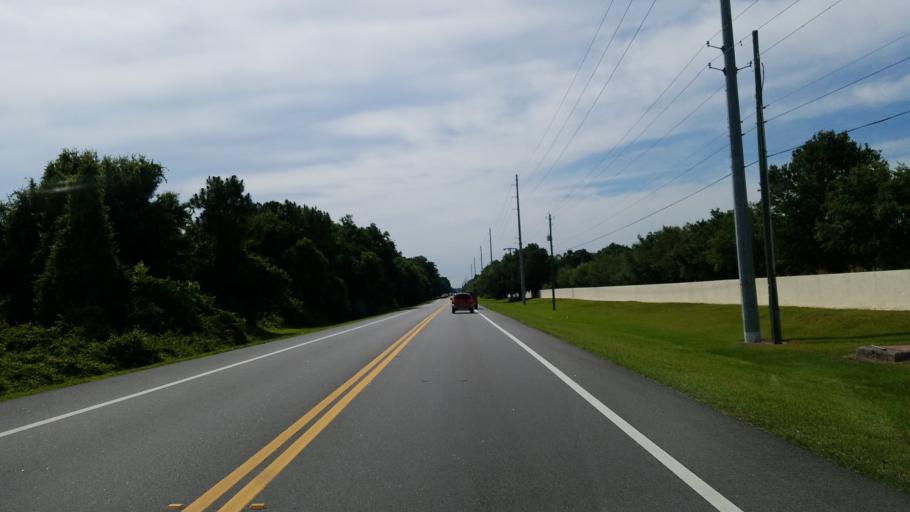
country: US
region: Florida
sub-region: Hillsborough County
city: Fish Hawk
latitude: 27.8513
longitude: -82.1827
